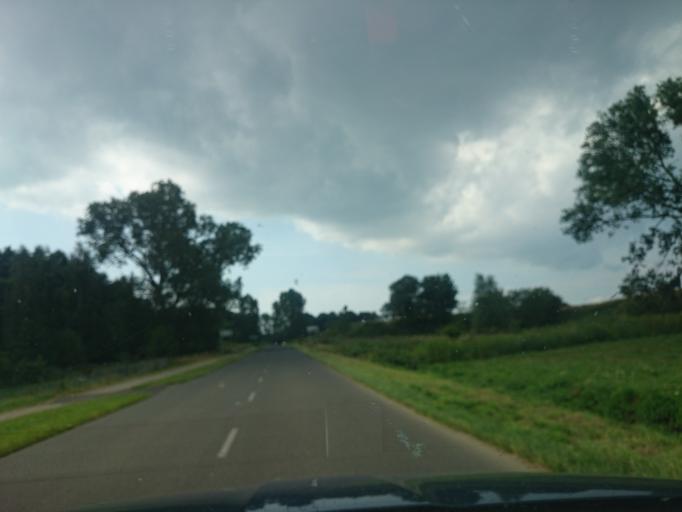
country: PL
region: West Pomeranian Voivodeship
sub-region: Powiat kamienski
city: Wolin
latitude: 53.9053
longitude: 14.6411
